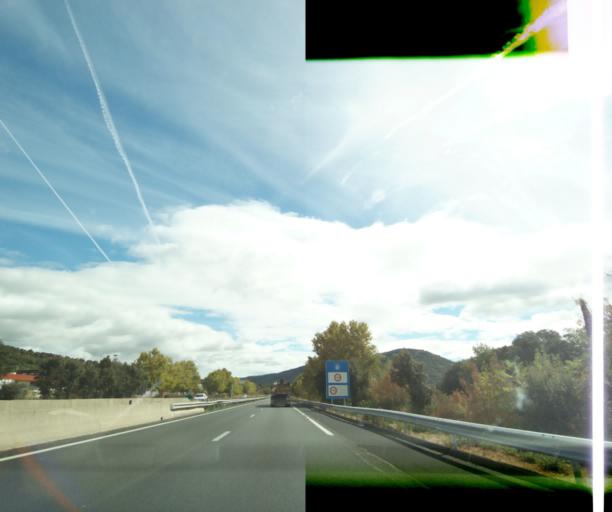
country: FR
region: Languedoc-Roussillon
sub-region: Departement de l'Herault
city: Lodeve
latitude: 43.6911
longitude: 3.3495
